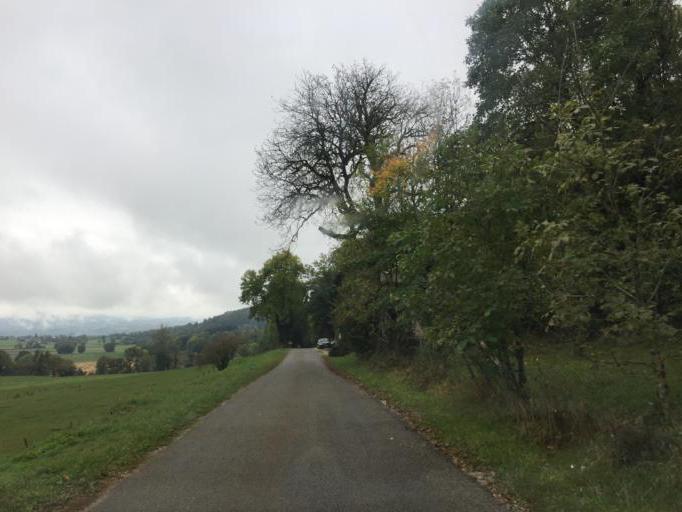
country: FR
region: Franche-Comte
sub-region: Departement du Jura
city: Orgelet
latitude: 46.5549
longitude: 5.6352
